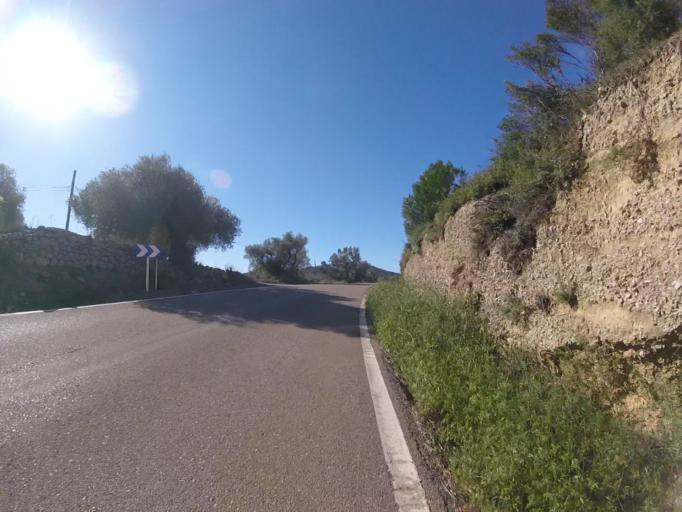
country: ES
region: Valencia
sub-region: Provincia de Castello
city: Chert/Xert
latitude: 40.4492
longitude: 0.1122
